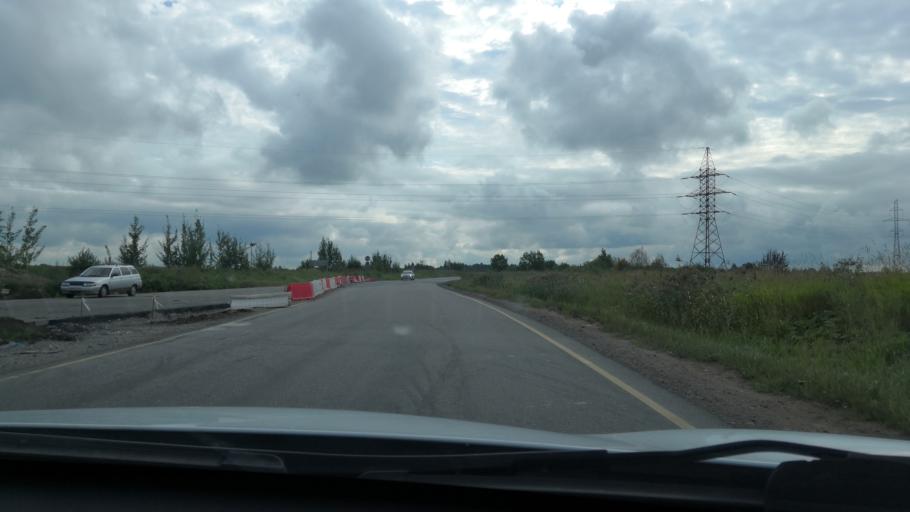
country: RU
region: Leningrad
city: Fedorovskoye
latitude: 59.7058
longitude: 30.5494
